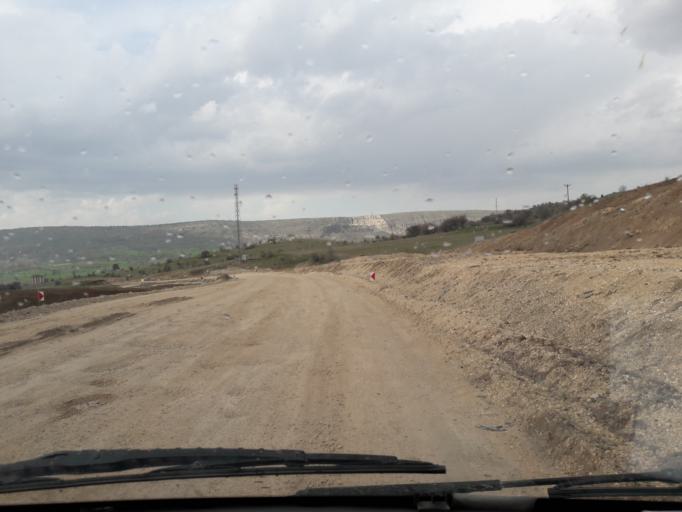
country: TR
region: Giresun
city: Alucra
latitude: 40.3181
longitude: 38.7732
